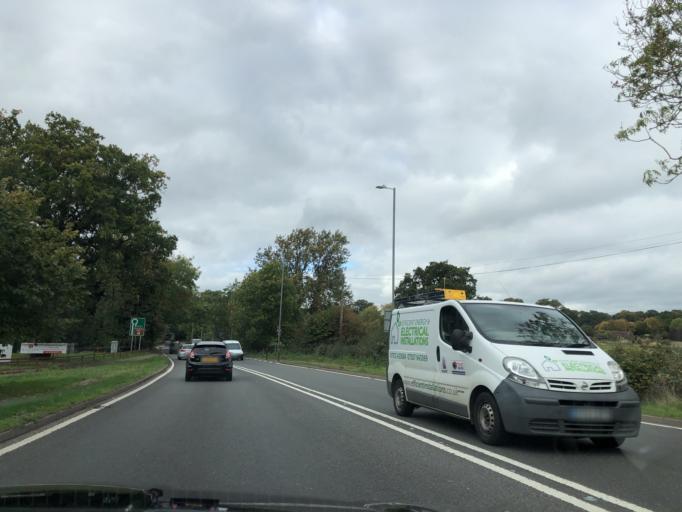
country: GB
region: England
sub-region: Warwickshire
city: Royal Leamington Spa
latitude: 52.3252
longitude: -1.5545
